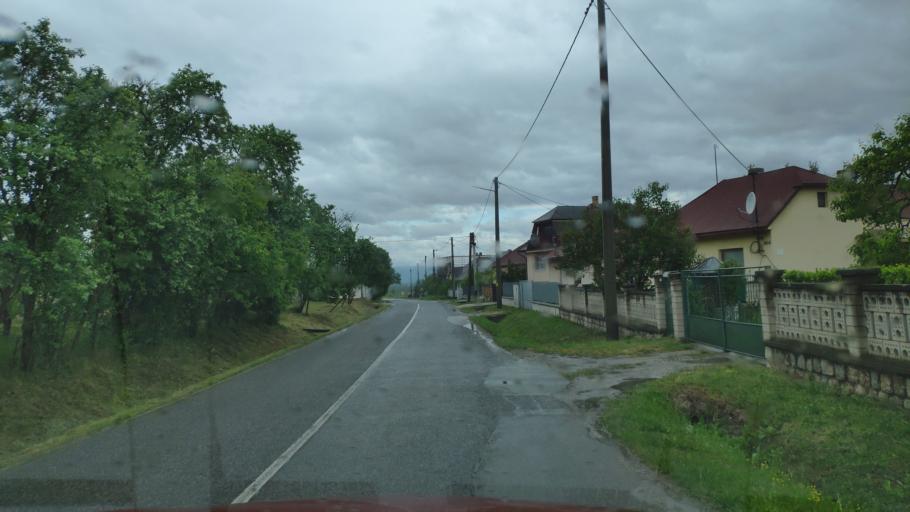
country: SK
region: Kosicky
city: Moldava nad Bodvou
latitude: 48.5351
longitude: 21.0761
